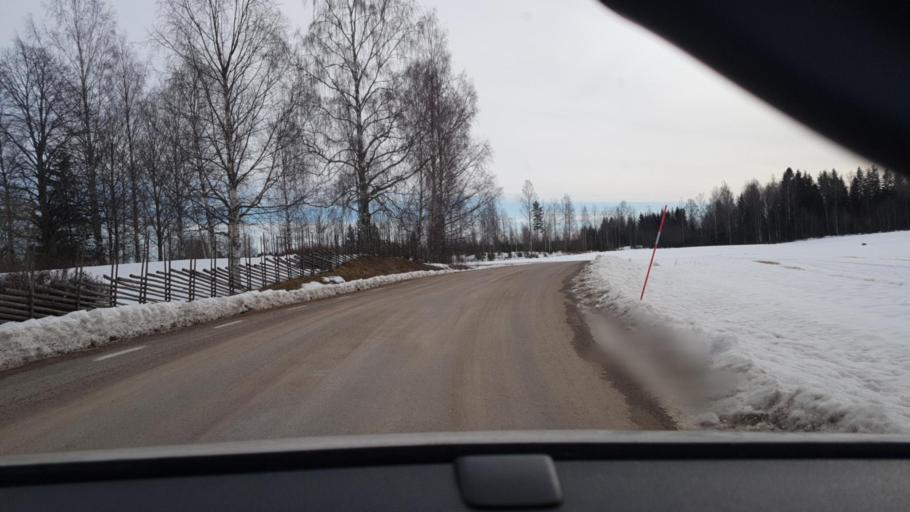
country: SE
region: Vaermland
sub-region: Eda Kommun
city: Amotfors
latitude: 59.7184
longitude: 12.4612
